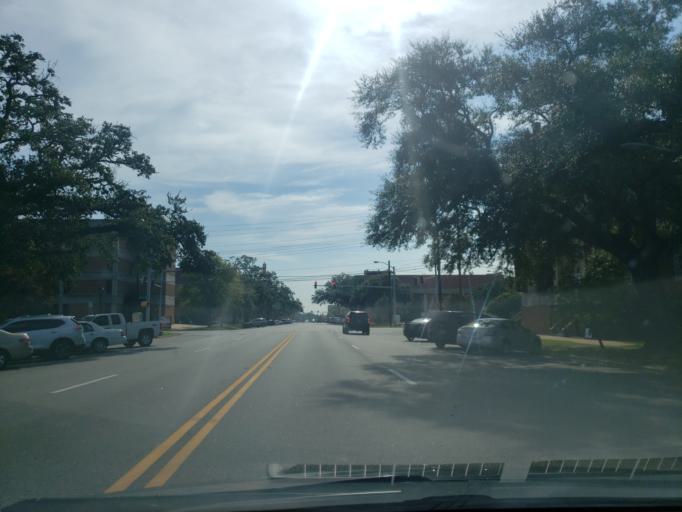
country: US
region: Georgia
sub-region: Dougherty County
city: Albany
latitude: 31.5784
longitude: -84.1567
